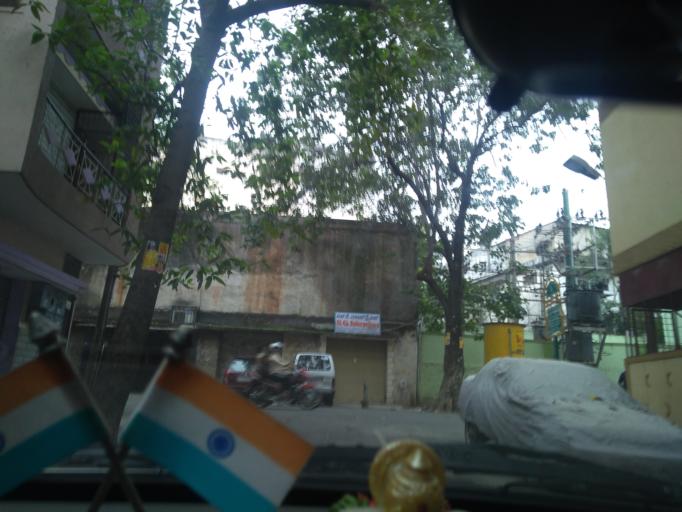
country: IN
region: Karnataka
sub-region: Bangalore Urban
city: Bangalore
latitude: 12.9773
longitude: 77.5522
